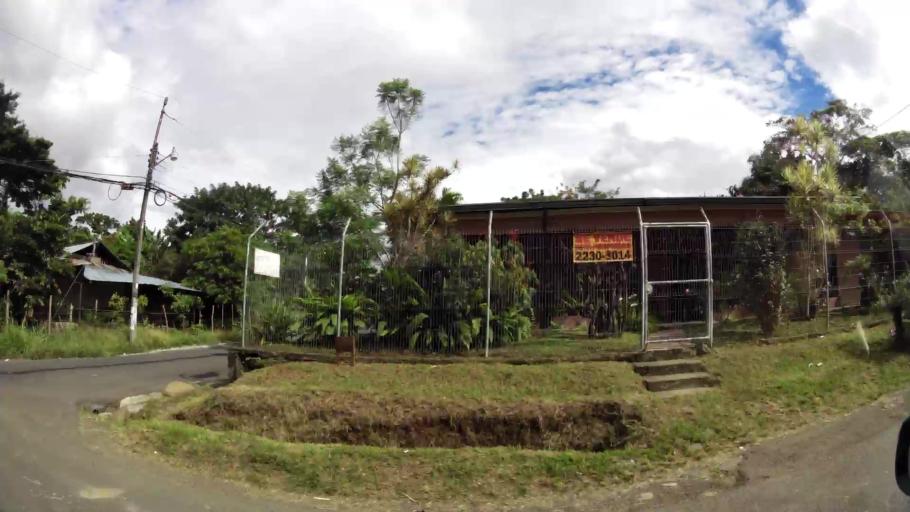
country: CR
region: San Jose
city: San Rafael Arriba
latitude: 9.8793
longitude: -84.0766
